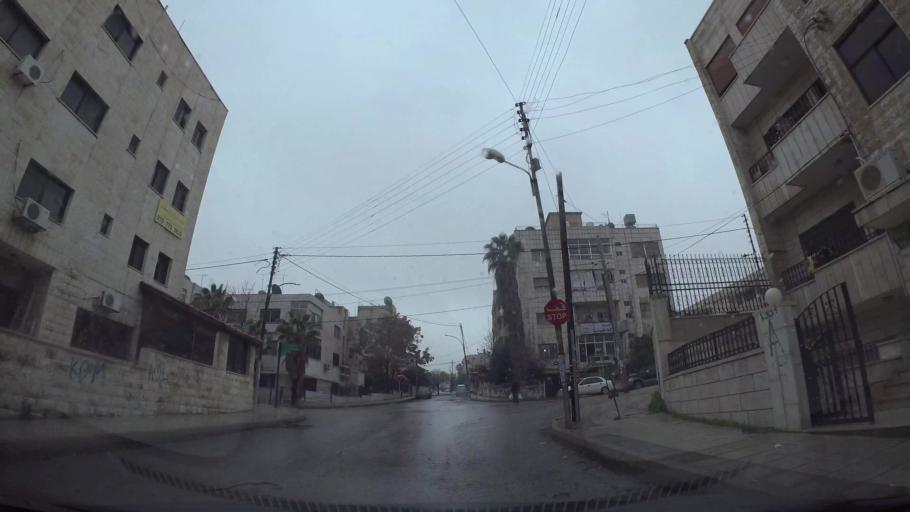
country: JO
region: Amman
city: Amman
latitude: 31.9752
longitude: 35.9166
